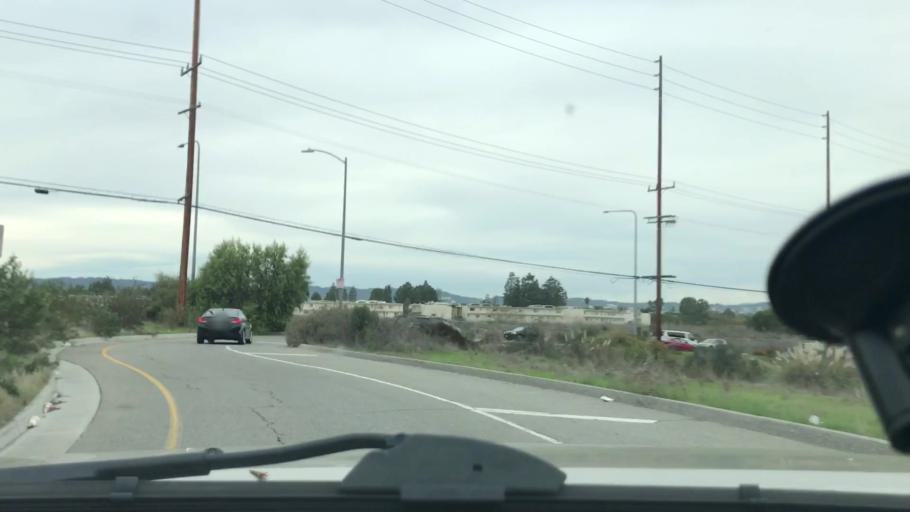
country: US
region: California
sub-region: Los Angeles County
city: Marina del Rey
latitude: 33.9765
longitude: -118.4318
